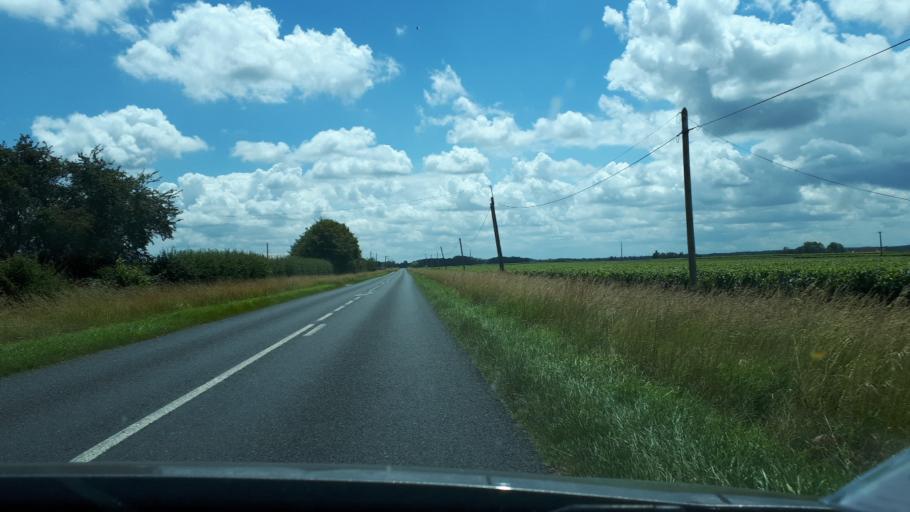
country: FR
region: Centre
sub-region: Departement du Loir-et-Cher
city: Contres
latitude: 47.3852
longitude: 1.4077
